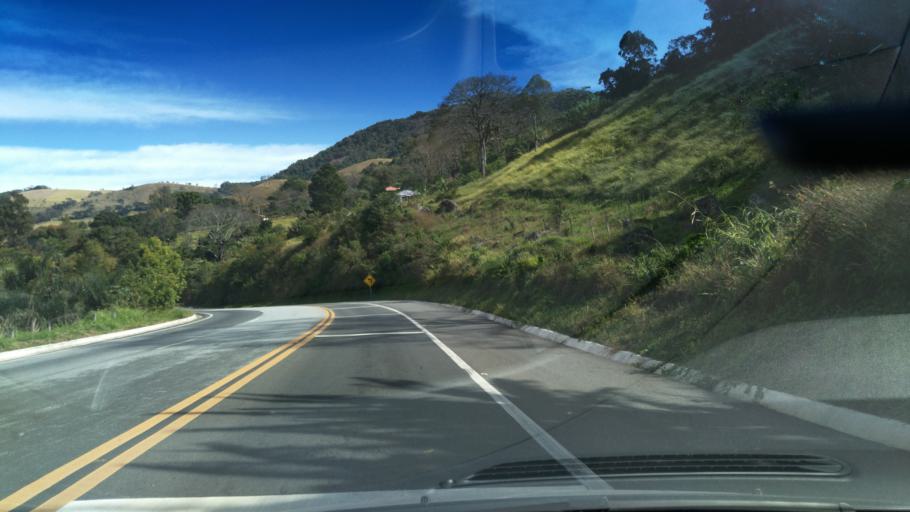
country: BR
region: Minas Gerais
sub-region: Borda Da Mata
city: Borda da Mata
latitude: -22.1316
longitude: -46.1754
